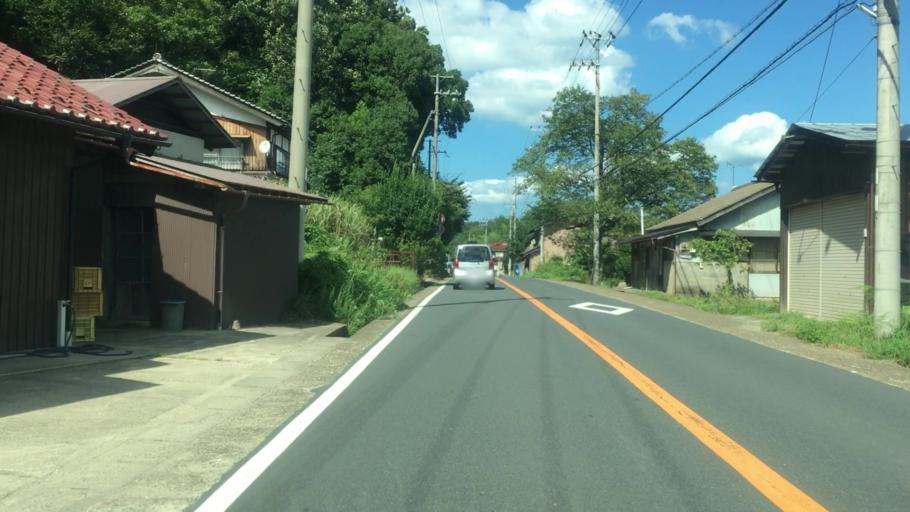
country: JP
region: Kyoto
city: Miyazu
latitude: 35.6108
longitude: 135.0534
